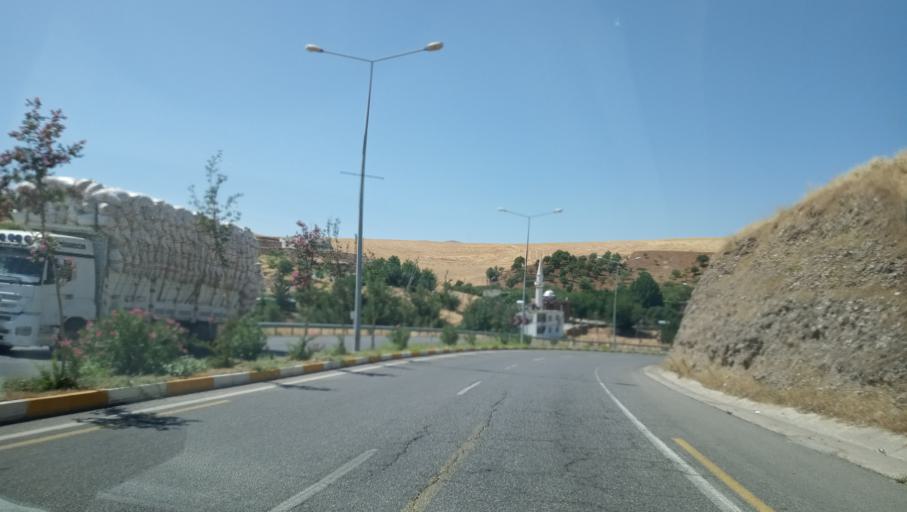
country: TR
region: Siirt
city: Civankan
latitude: 37.9490
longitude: 41.8767
